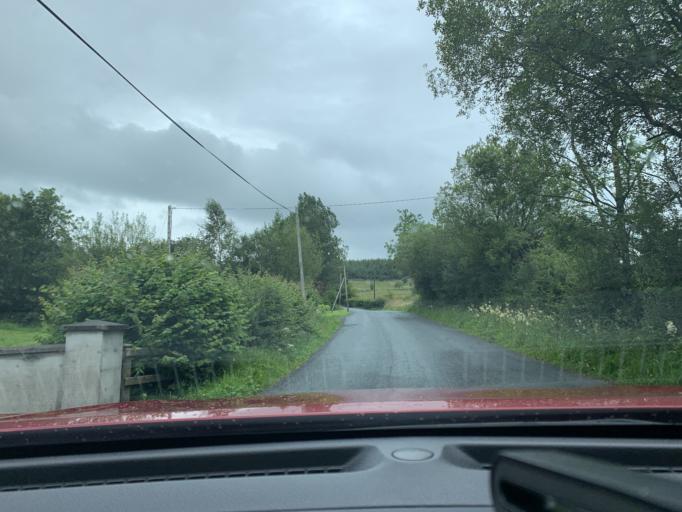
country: IE
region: Connaught
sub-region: County Leitrim
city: Manorhamilton
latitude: 54.3098
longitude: -8.2244
